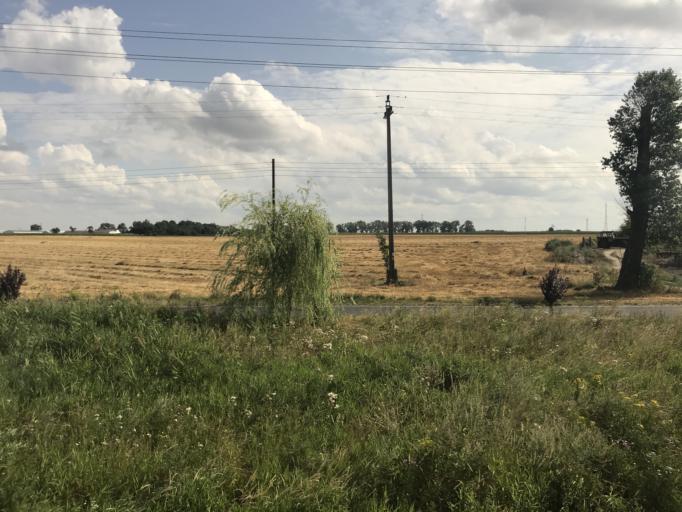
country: PL
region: Kujawsko-Pomorskie
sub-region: Powiat inowroclawski
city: Zlotniki Kujawskie
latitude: 52.9008
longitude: 18.1505
